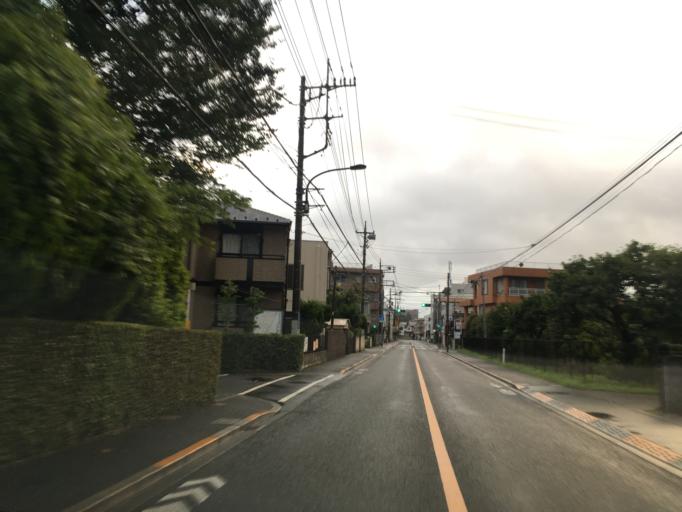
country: JP
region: Tokyo
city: Kokubunji
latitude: 35.6905
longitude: 139.5019
